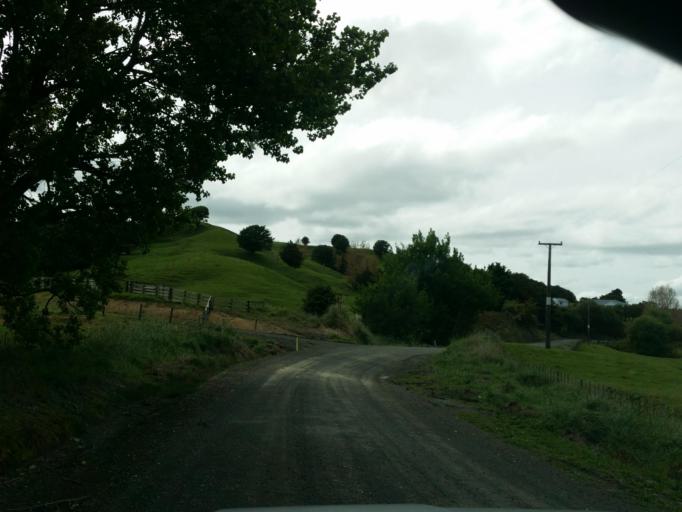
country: NZ
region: Northland
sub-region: Whangarei
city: Maungatapere
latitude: -35.9017
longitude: 174.1437
